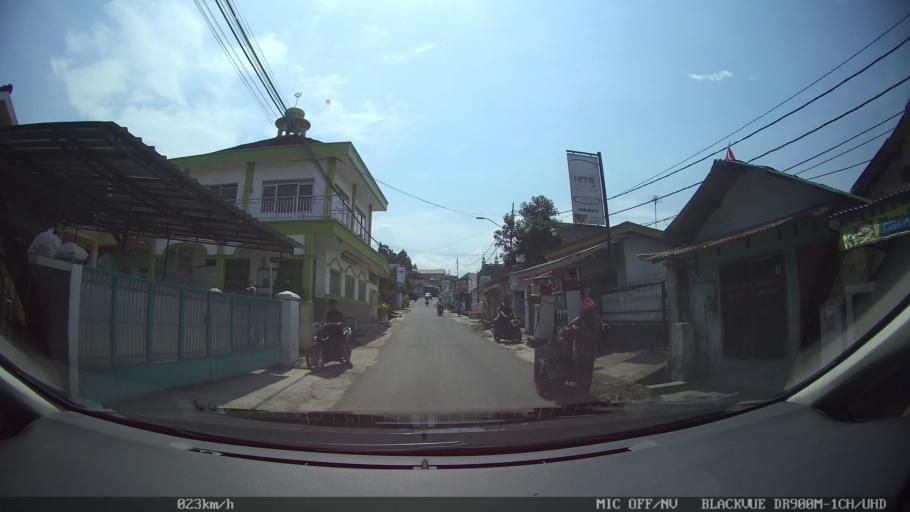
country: ID
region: Lampung
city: Kedaton
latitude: -5.3977
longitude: 105.2563
